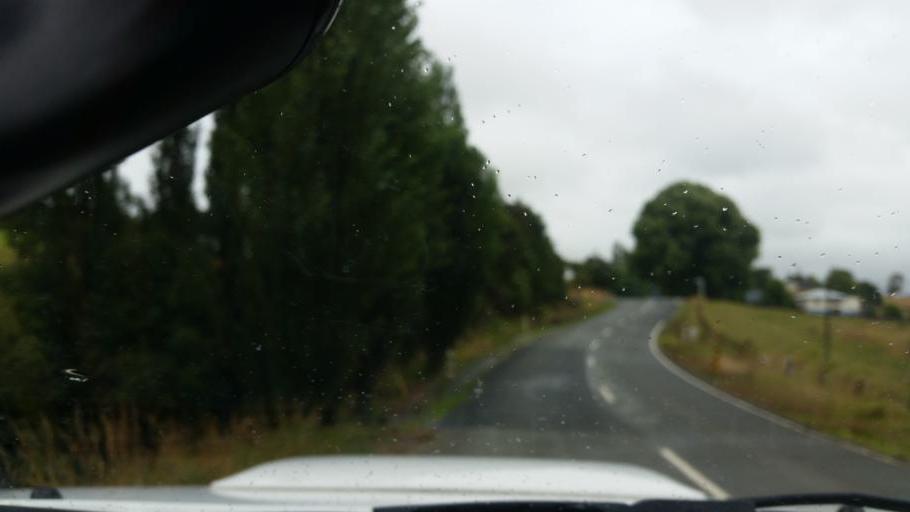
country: NZ
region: Auckland
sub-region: Auckland
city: Wellsford
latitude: -36.1703
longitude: 174.4682
